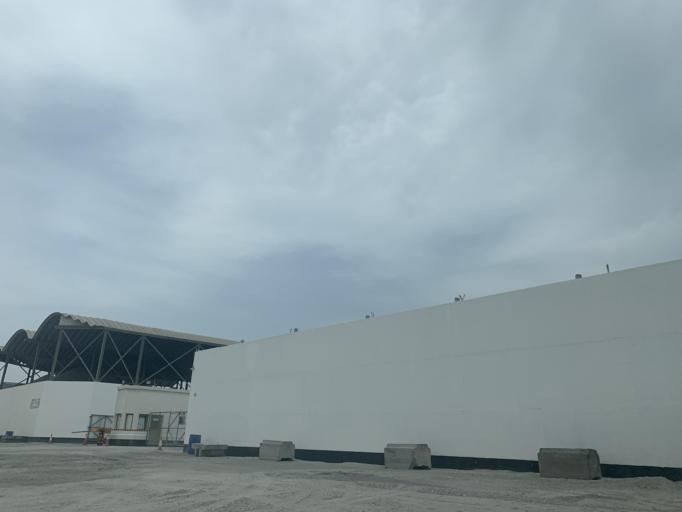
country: BH
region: Muharraq
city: Al Hadd
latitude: 26.2043
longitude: 50.6711
